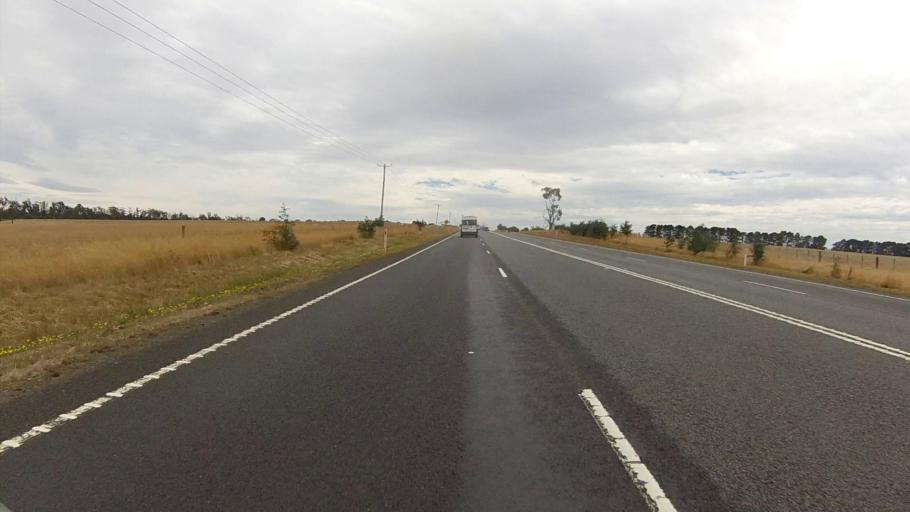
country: AU
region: Tasmania
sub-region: Northern Midlands
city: Evandale
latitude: -41.7140
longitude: 147.3050
